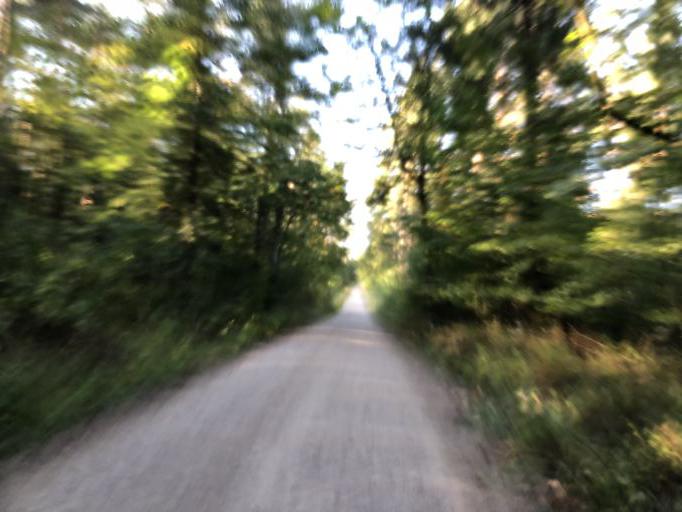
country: DE
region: Bavaria
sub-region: Regierungsbezirk Mittelfranken
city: Kalchreuth
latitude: 49.5498
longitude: 11.1004
